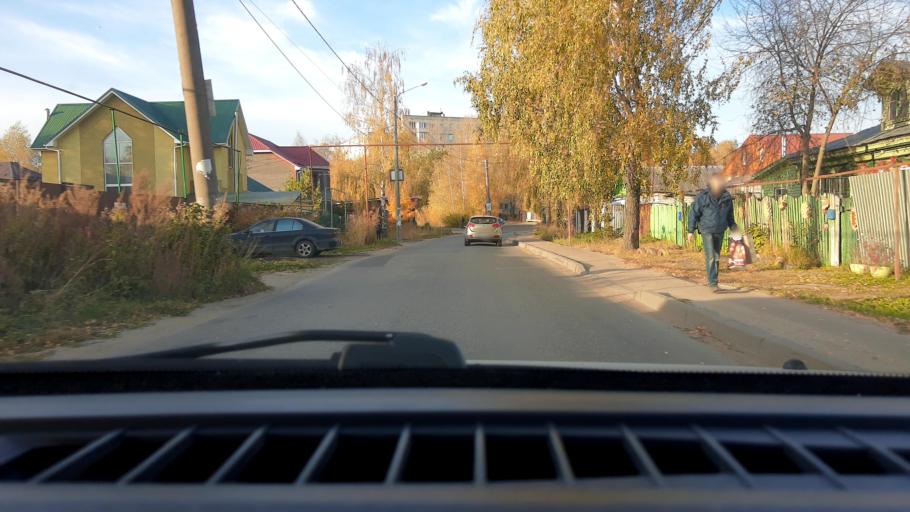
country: RU
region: Nizjnij Novgorod
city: Gorbatovka
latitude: 56.3382
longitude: 43.8304
